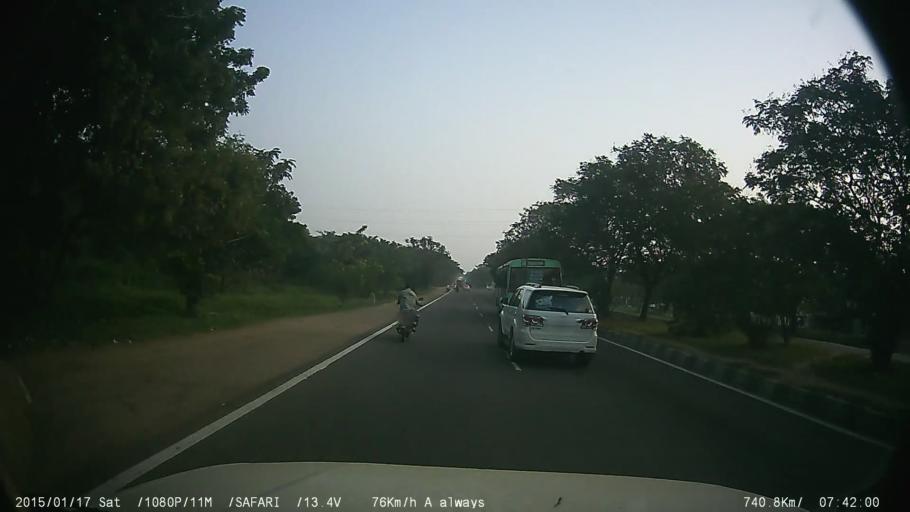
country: IN
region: Tamil Nadu
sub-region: Kancheepuram
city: Singapperumalkovil
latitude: 12.8004
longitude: 80.0235
